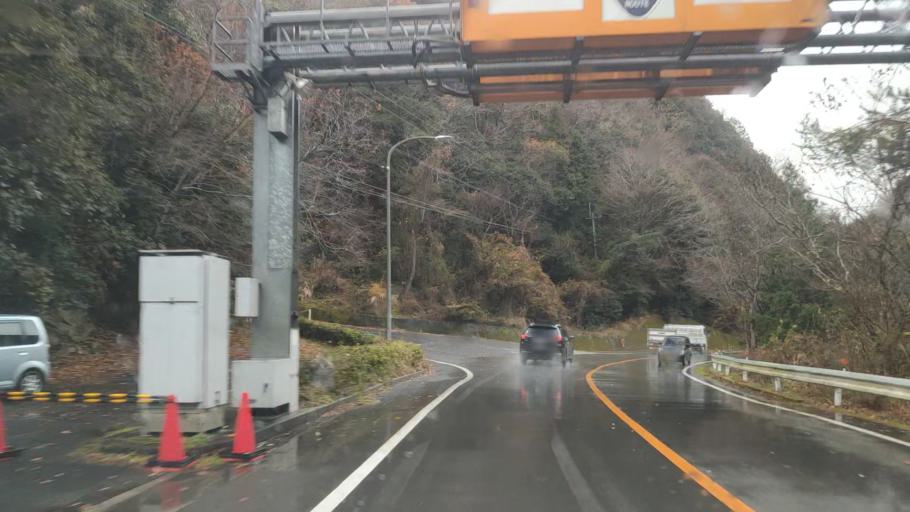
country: JP
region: Tokushima
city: Kamojimacho-jogejima
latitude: 34.1644
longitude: 134.3339
